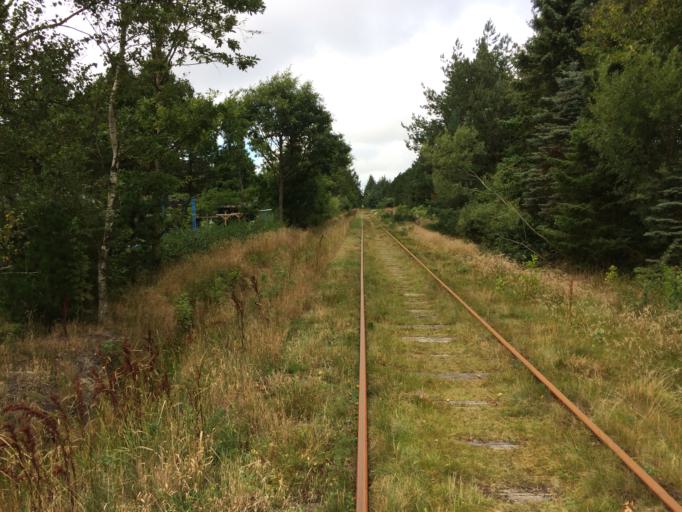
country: DK
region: South Denmark
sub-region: Varde Kommune
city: Oksbol
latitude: 55.7946
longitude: 8.2274
